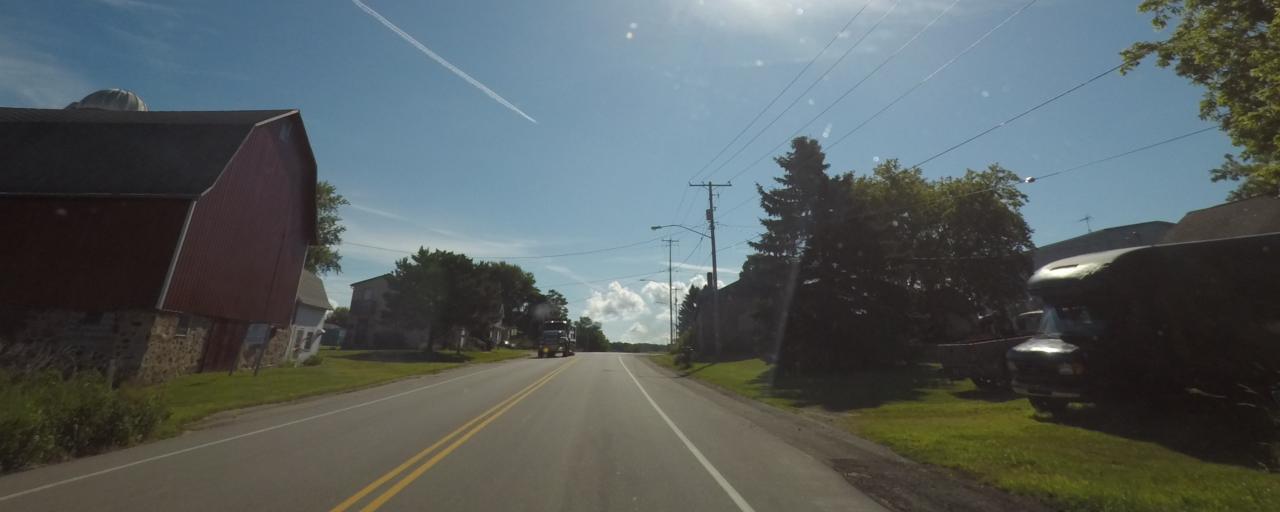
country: US
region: Wisconsin
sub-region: Jefferson County
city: Johnson Creek
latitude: 43.0760
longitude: -88.6734
